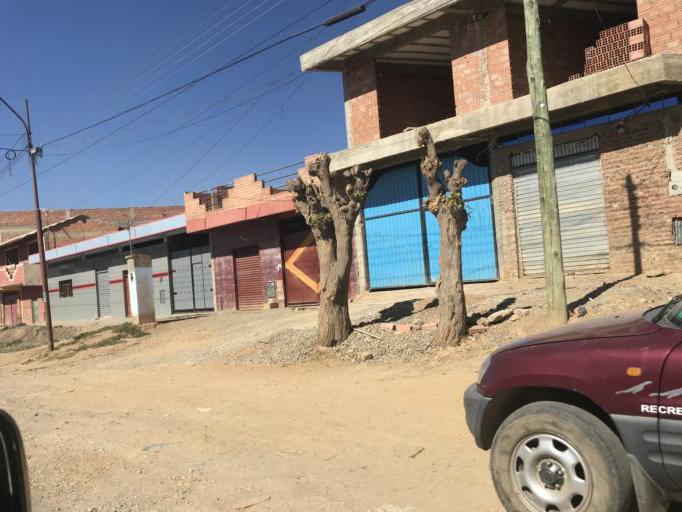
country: BO
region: Cochabamba
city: Cliza
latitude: -17.5855
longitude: -65.9186
